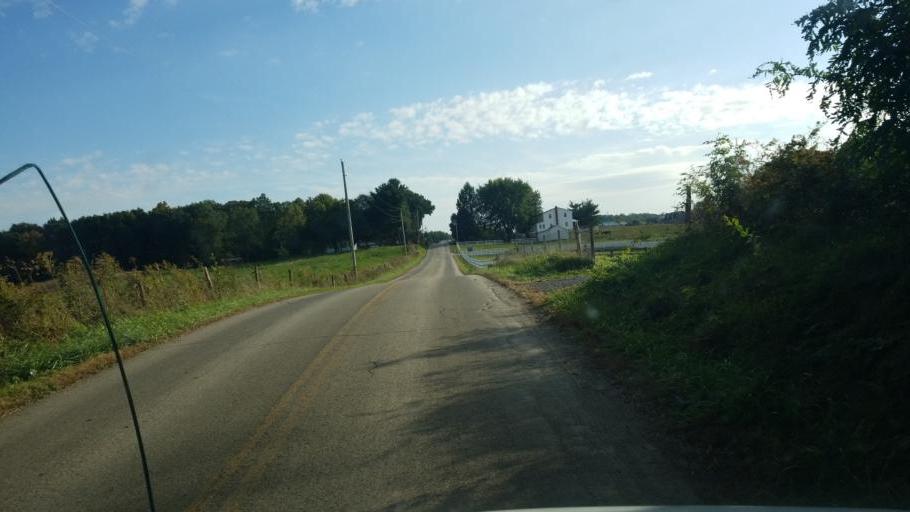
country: US
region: Ohio
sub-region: Wayne County
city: Shreve
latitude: 40.6350
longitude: -82.0814
